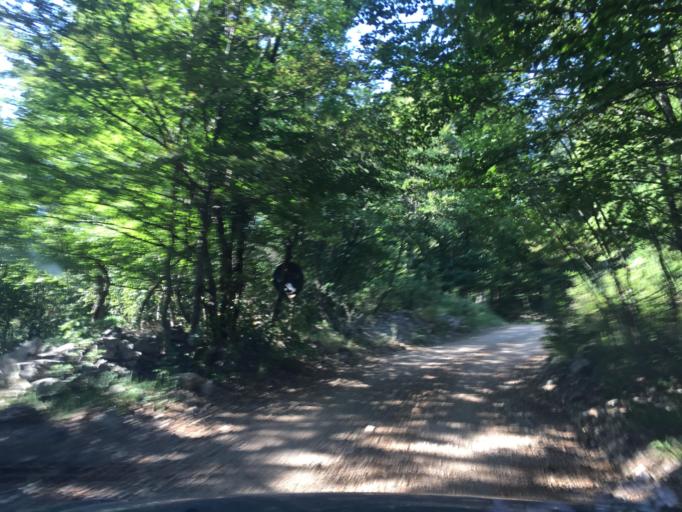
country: HR
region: Primorsko-Goranska
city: Klana
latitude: 45.4401
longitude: 14.4040
